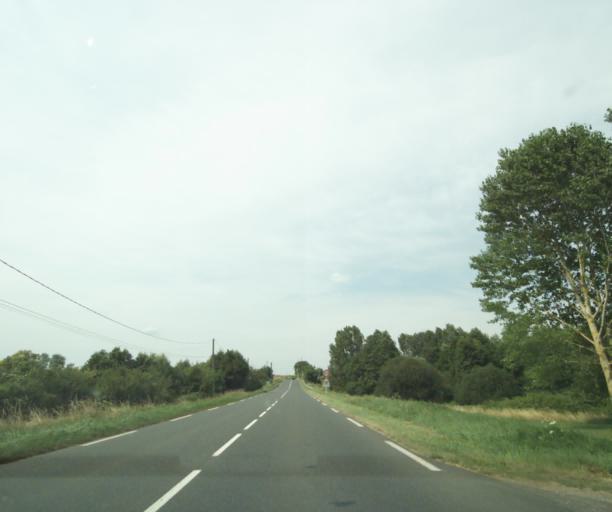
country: FR
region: Centre
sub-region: Departement d'Indre-et-Loire
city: Neuille-Pont-Pierre
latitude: 47.5612
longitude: 0.5496
